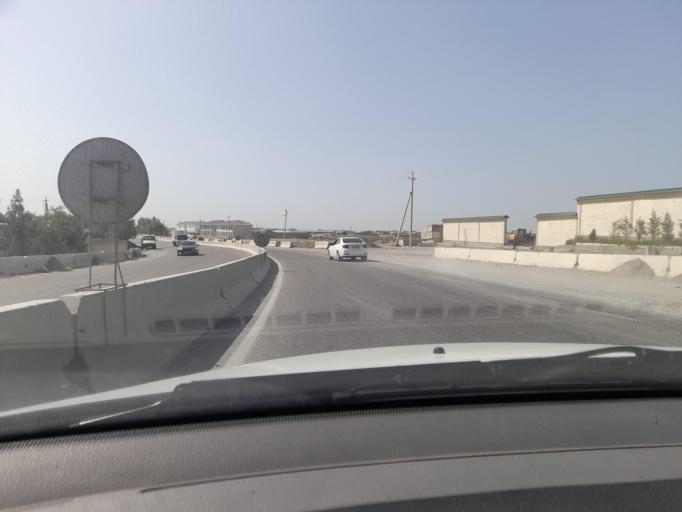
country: UZ
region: Samarqand
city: Samarqand
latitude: 39.6994
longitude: 67.0183
